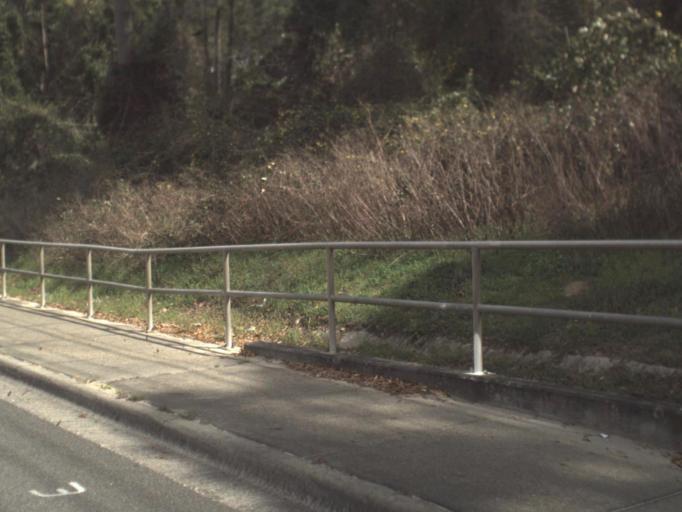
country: US
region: Florida
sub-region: Leon County
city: Tallahassee
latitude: 30.5206
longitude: -84.2390
